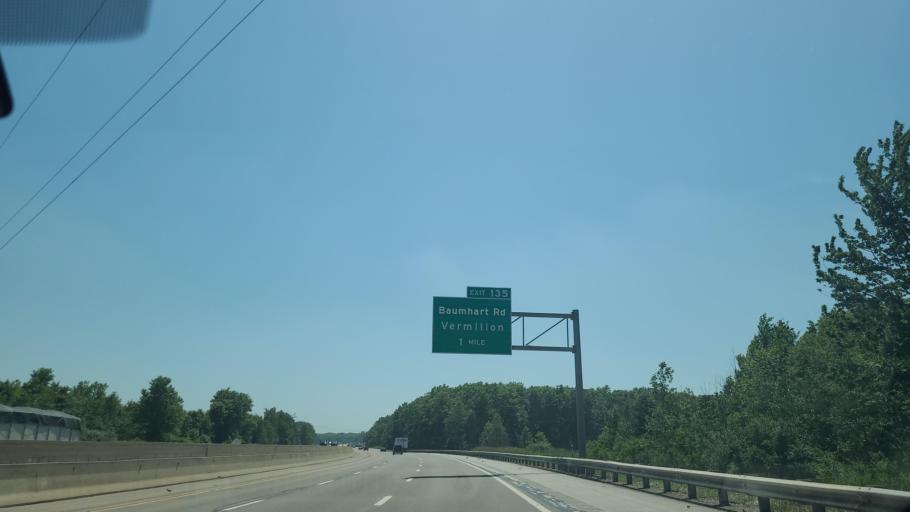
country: US
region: Ohio
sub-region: Lorain County
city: South Amherst
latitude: 41.3740
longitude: -82.2656
